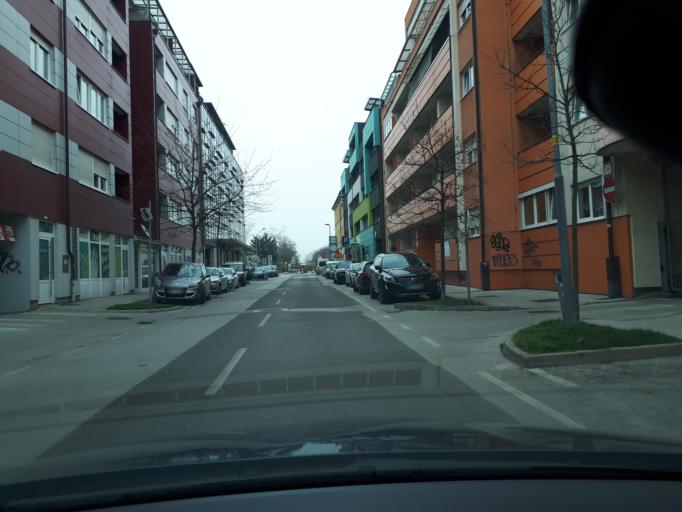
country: SI
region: Maribor
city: Maribor
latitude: 46.5511
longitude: 15.6421
